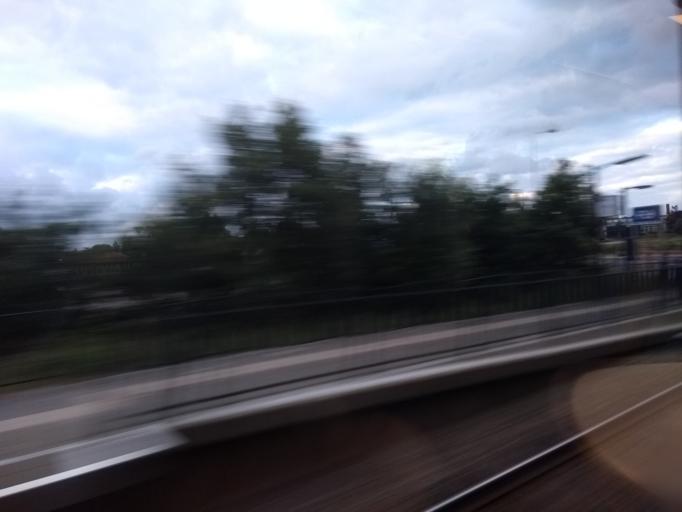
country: NL
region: Friesland
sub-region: Gemeente Heerenveen
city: Oranjewoud
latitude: 52.9358
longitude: 5.9437
